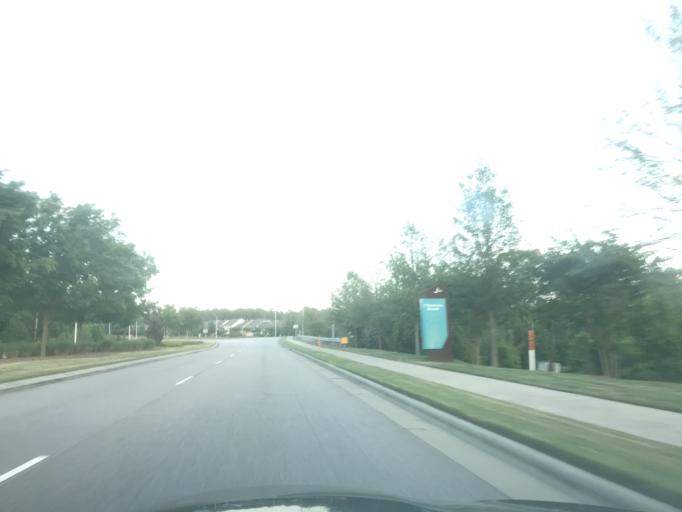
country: US
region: North Carolina
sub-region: Wake County
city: Wendell
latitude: 35.7703
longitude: -78.4247
